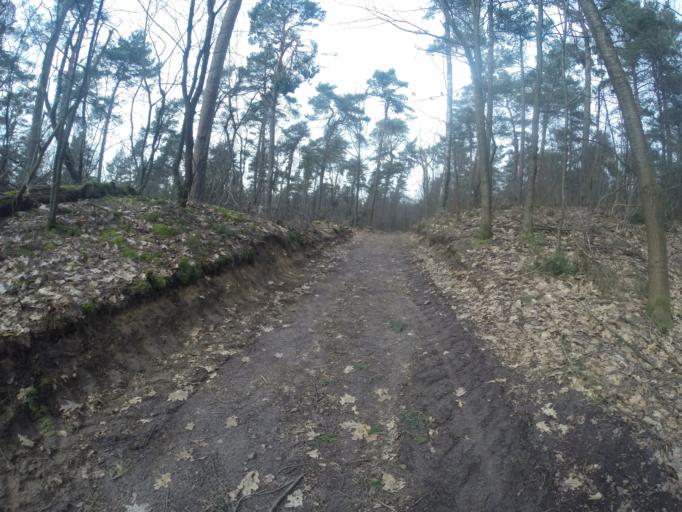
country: NL
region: Gelderland
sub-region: Gemeente Bronckhorst
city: Zelhem
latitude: 52.0411
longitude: 6.3835
